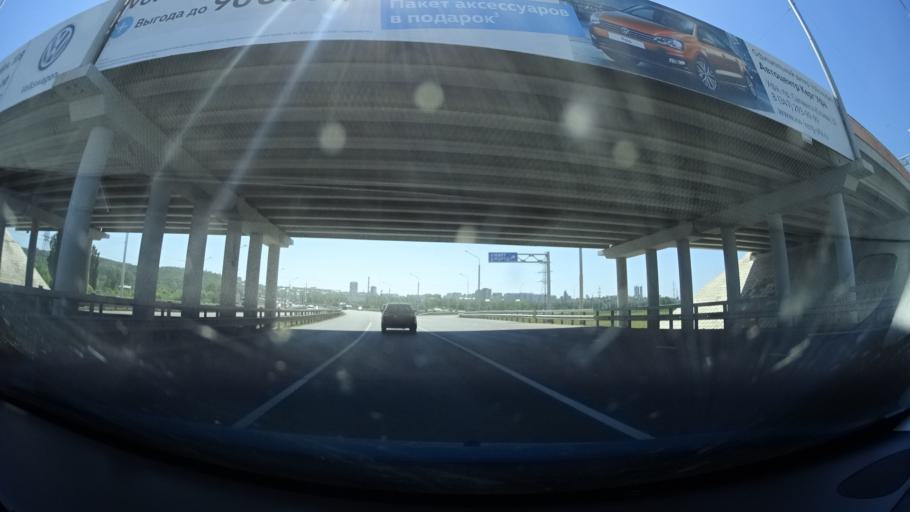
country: RU
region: Bashkortostan
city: Ufa
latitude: 54.7648
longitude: 55.9556
